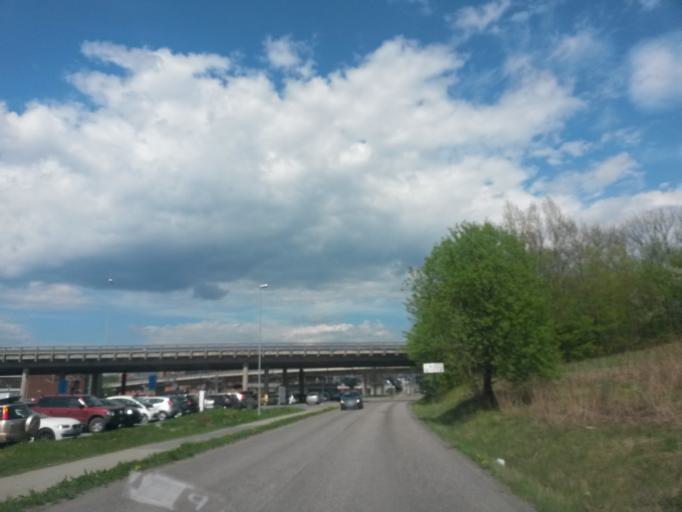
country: NO
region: Akershus
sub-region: Asker
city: Asker
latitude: 59.8309
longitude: 10.4336
